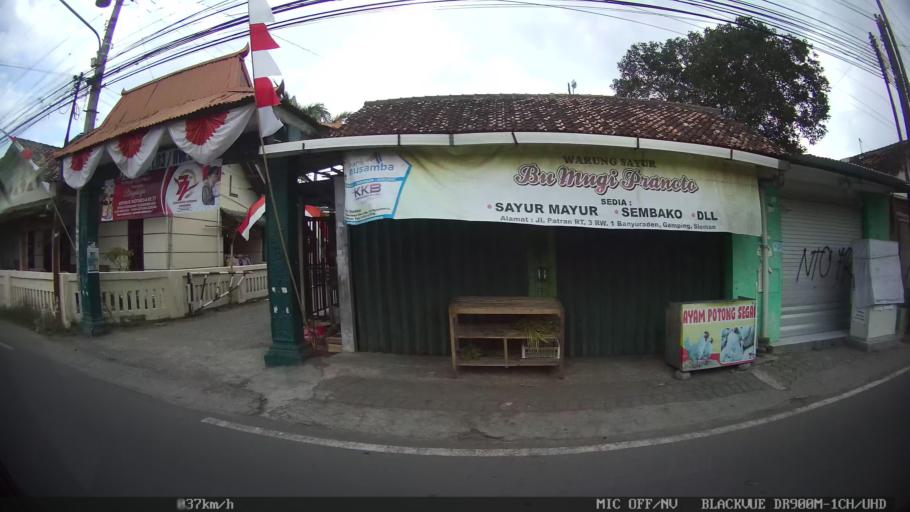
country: ID
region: Daerah Istimewa Yogyakarta
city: Gamping Lor
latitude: -7.7828
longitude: 110.3403
